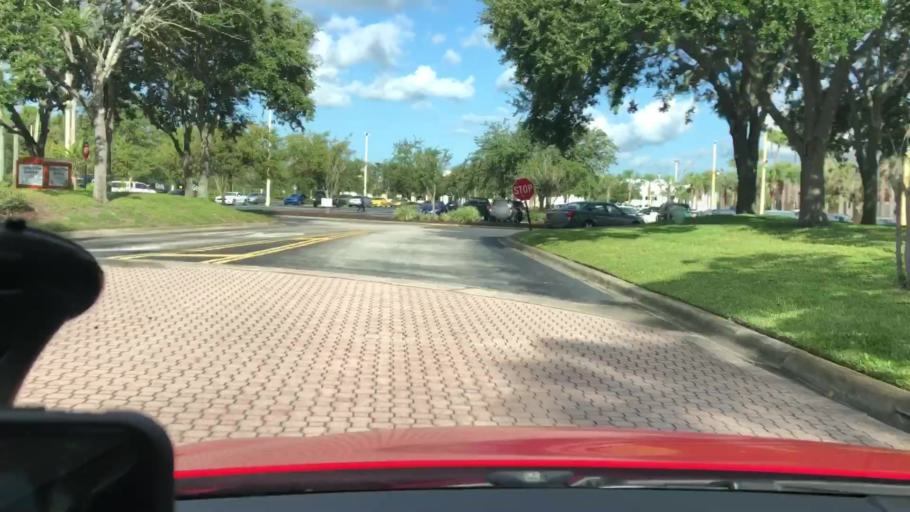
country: US
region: Florida
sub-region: Volusia County
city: Daytona Beach
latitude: 29.1908
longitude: -81.0740
